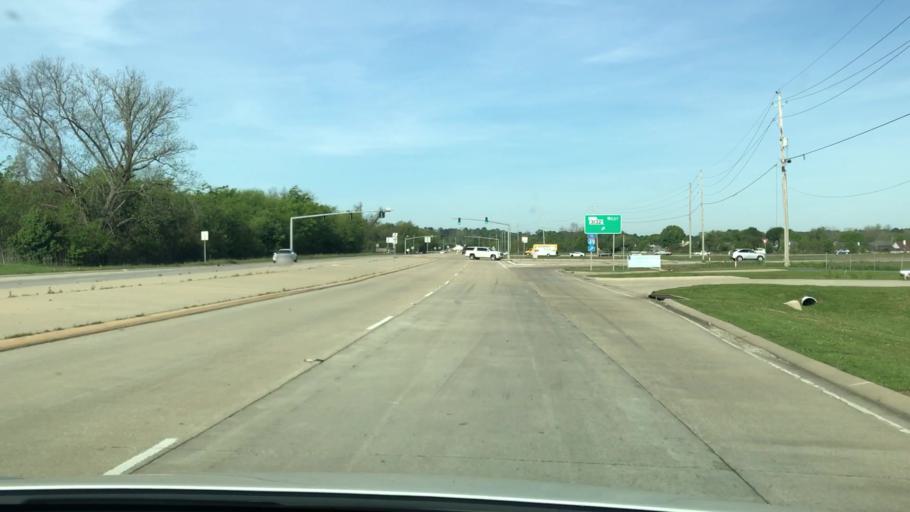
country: US
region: Louisiana
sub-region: Bossier Parish
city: Bossier City
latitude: 32.4009
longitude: -93.7124
